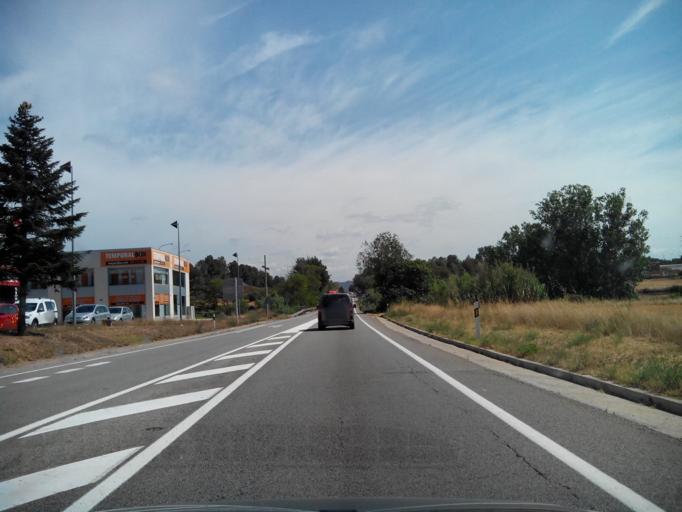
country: ES
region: Catalonia
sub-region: Provincia de Barcelona
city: Sant Fruitos de Bages
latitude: 41.7524
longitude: 1.8643
